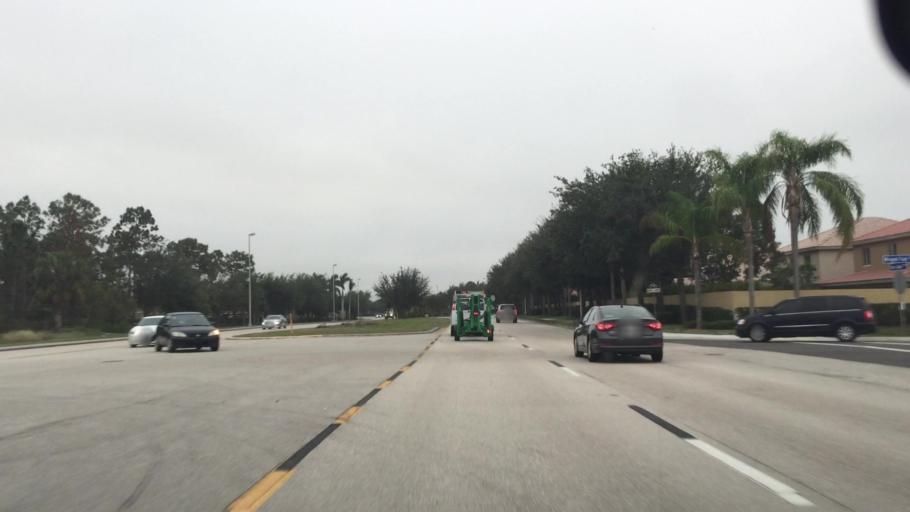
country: US
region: Florida
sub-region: Lee County
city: Three Oaks
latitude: 26.4861
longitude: -81.7990
